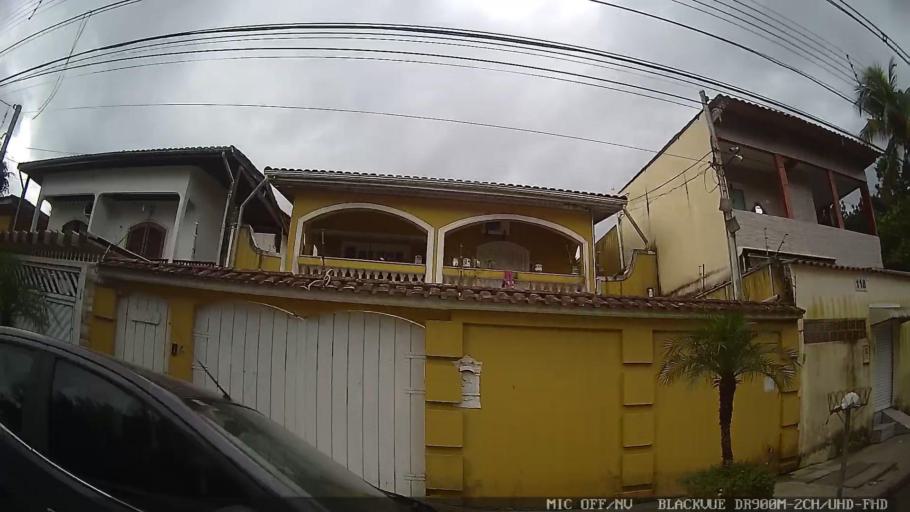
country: BR
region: Sao Paulo
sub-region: Guaruja
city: Guaruja
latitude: -23.9956
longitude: -46.2720
